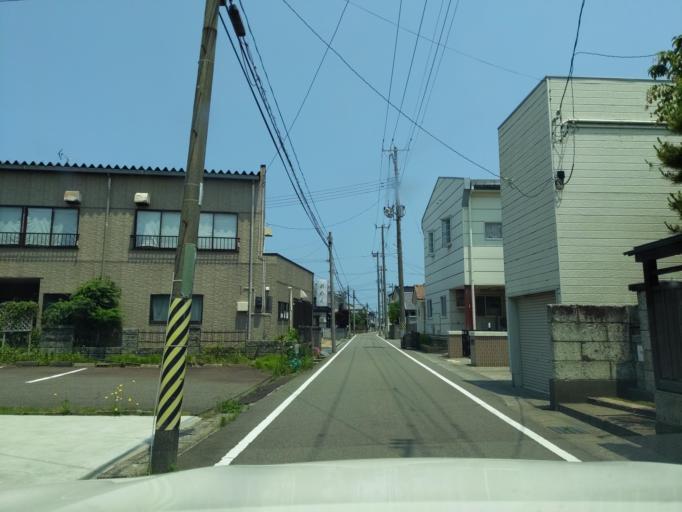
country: JP
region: Niigata
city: Kashiwazaki
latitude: 37.3726
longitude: 138.5640
